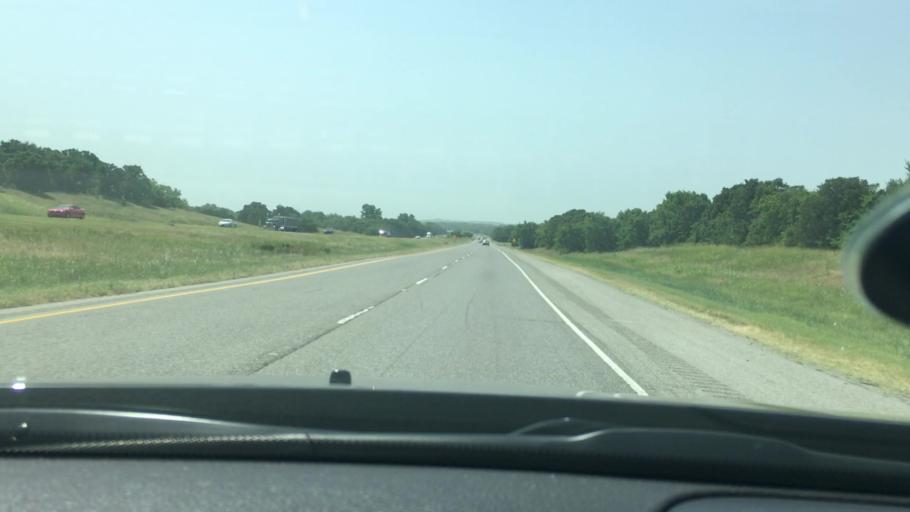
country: US
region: Oklahoma
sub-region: Murray County
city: Davis
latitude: 34.5400
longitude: -97.1893
